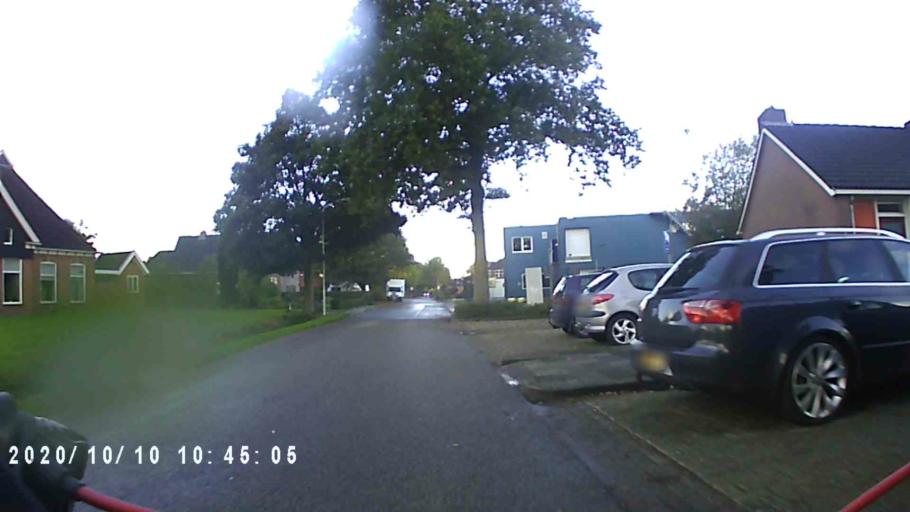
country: NL
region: Groningen
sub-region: Gemeente Grootegast
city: Grootegast
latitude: 53.1710
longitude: 6.2589
